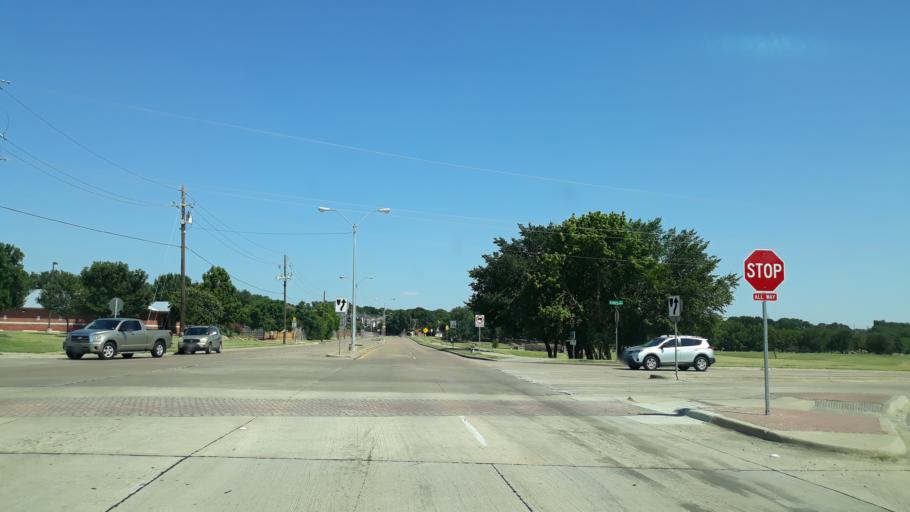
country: US
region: Texas
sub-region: Dallas County
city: Irving
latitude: 32.8239
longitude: -97.0111
